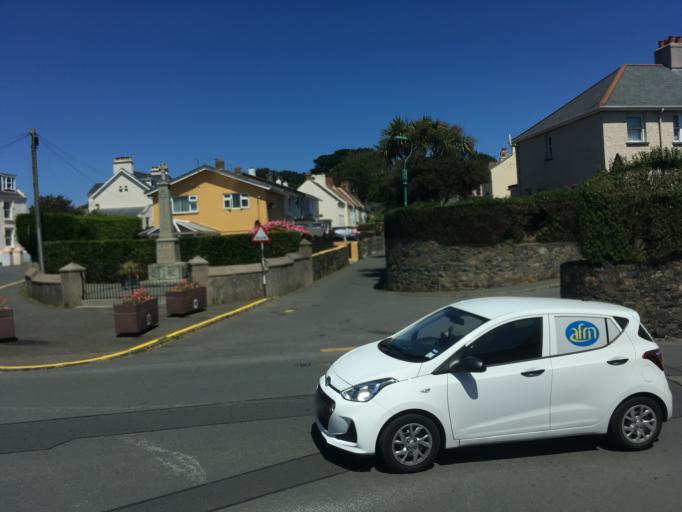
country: GG
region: St Peter Port
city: Saint Peter Port
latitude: 49.4866
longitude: -2.5192
